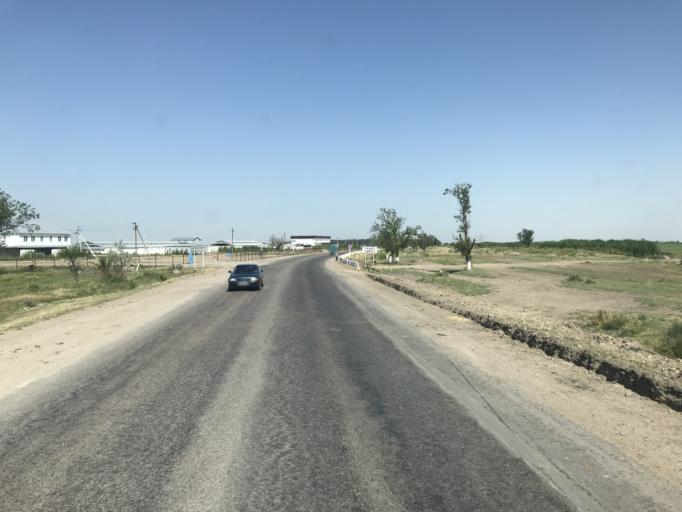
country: KZ
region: Zhambyl
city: Taraz
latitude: 42.9536
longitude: 71.2838
